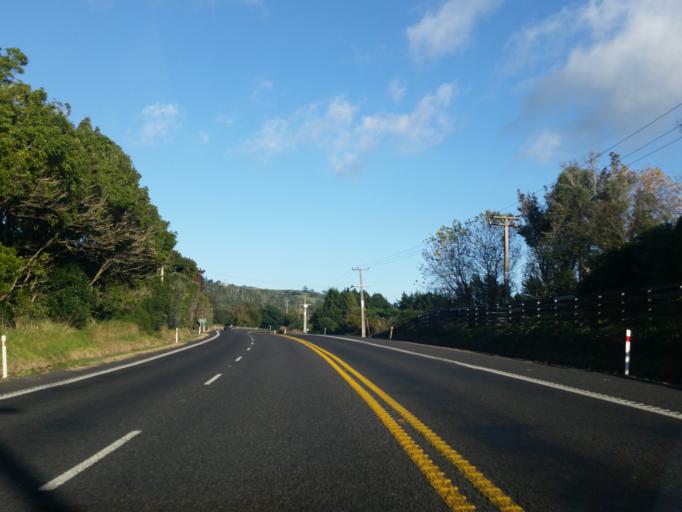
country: NZ
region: Bay of Plenty
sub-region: Tauranga City
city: Tauranga
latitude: -37.6970
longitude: 176.0608
